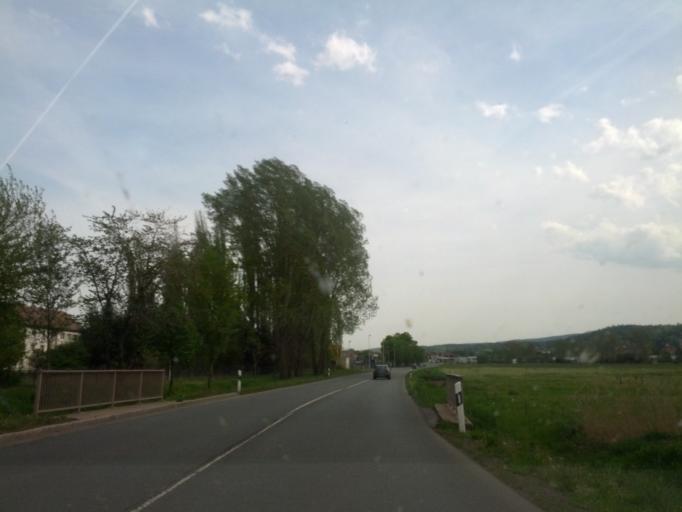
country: DE
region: Thuringia
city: Waltershausen
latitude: 50.9119
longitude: 10.5543
